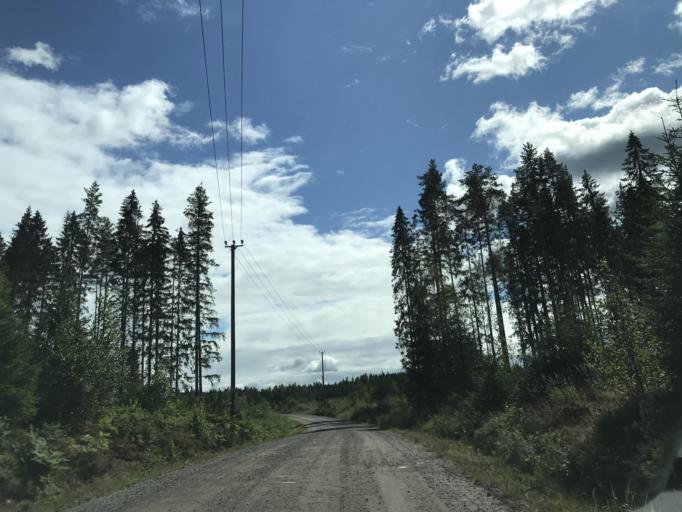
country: FI
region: Uusimaa
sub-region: Helsinki
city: Kaerkoelae
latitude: 60.6369
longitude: 23.8272
